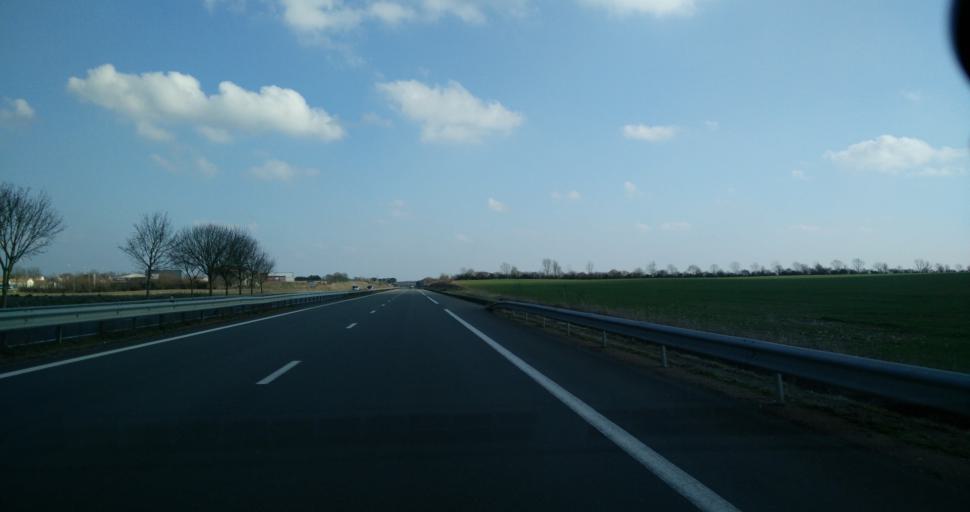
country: FR
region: Poitou-Charentes
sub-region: Departement de la Charente-Maritime
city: Saint-Jean-de-Liversay
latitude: 46.2265
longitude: -0.8743
